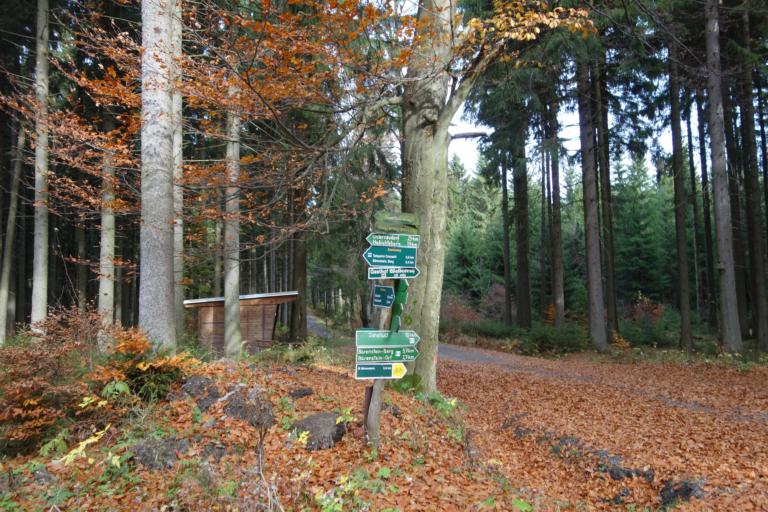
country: CZ
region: Ustecky
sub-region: Okres Chomutov
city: Vejprty
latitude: 50.4928
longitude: 12.9995
